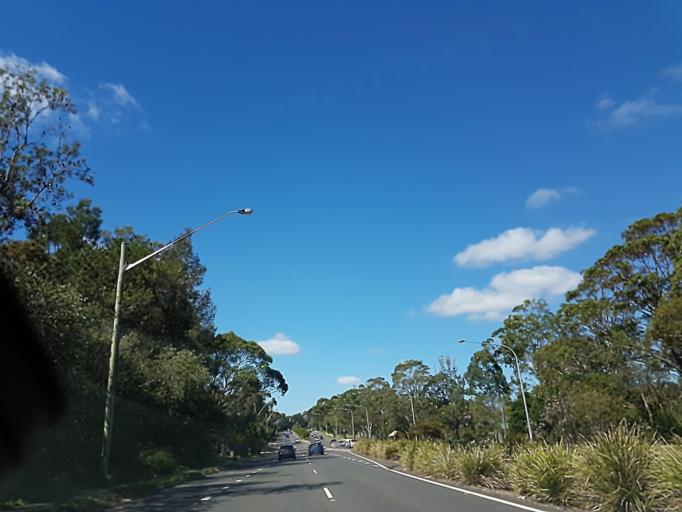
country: AU
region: New South Wales
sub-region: Warringah
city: Davidson
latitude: -33.7268
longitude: 151.2205
